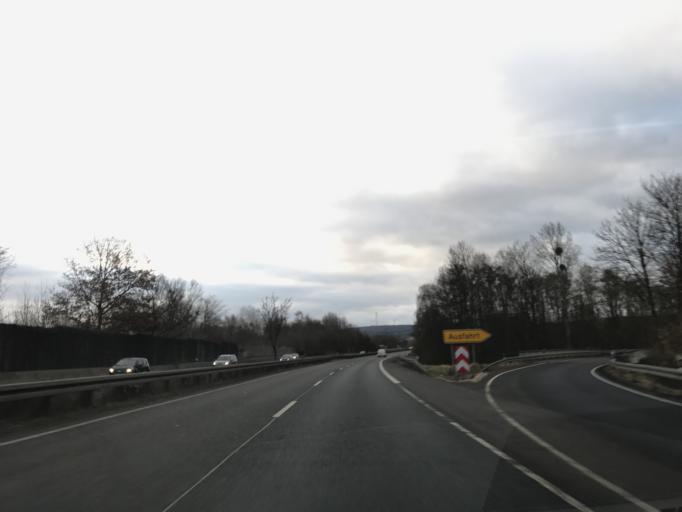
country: DE
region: Hesse
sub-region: Regierungsbezirk Kassel
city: Kaufungen
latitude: 51.2877
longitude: 9.5849
